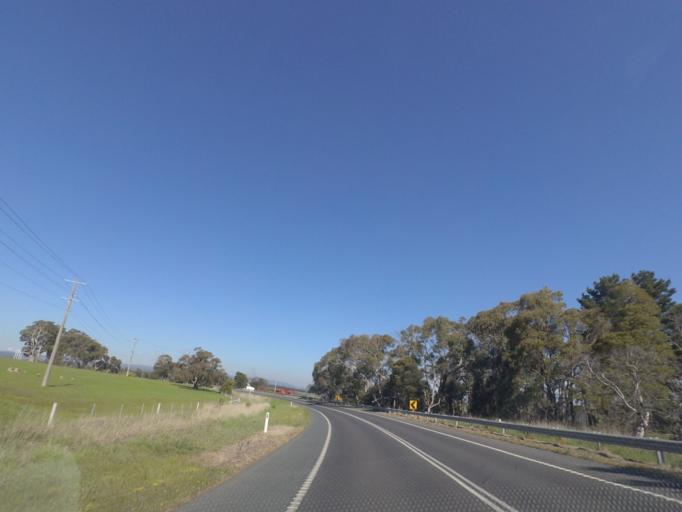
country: AU
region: Victoria
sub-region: Whittlesea
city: Whittlesea
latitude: -37.3376
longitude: 144.9830
